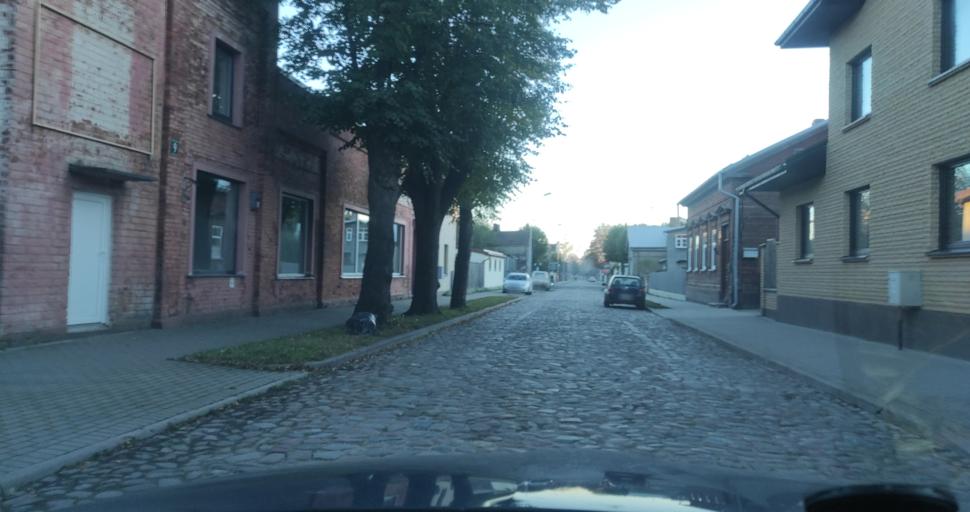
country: LV
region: Liepaja
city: Liepaja
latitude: 56.5019
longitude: 21.0120
